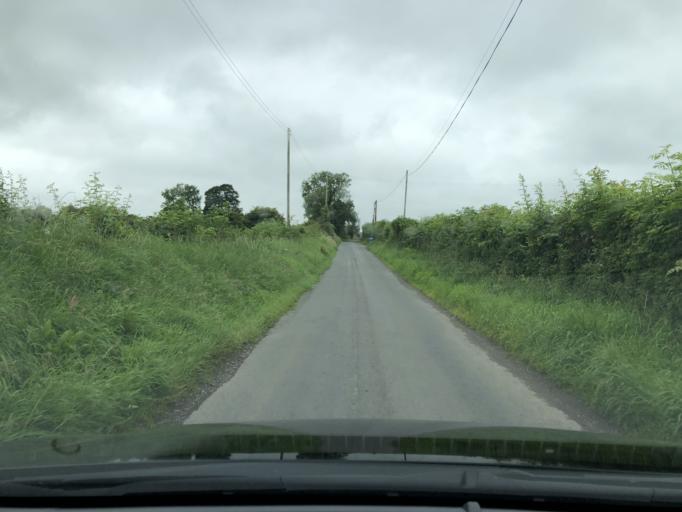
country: GB
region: Northern Ireland
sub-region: Down District
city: Dundrum
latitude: 54.3032
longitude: -5.8512
